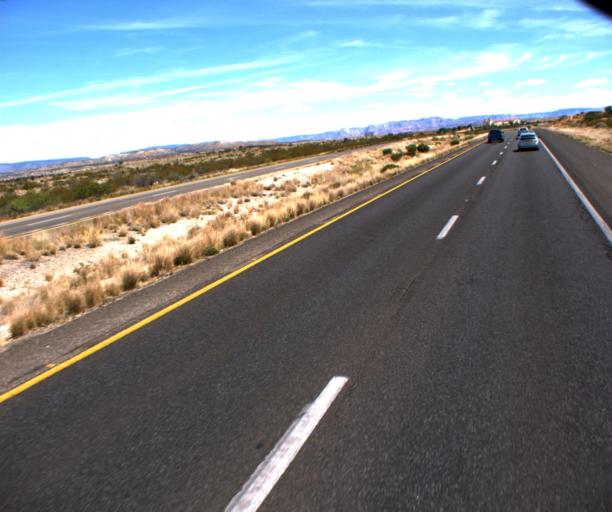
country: US
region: Arizona
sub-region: Yavapai County
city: Cottonwood
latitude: 34.7347
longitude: -111.9764
